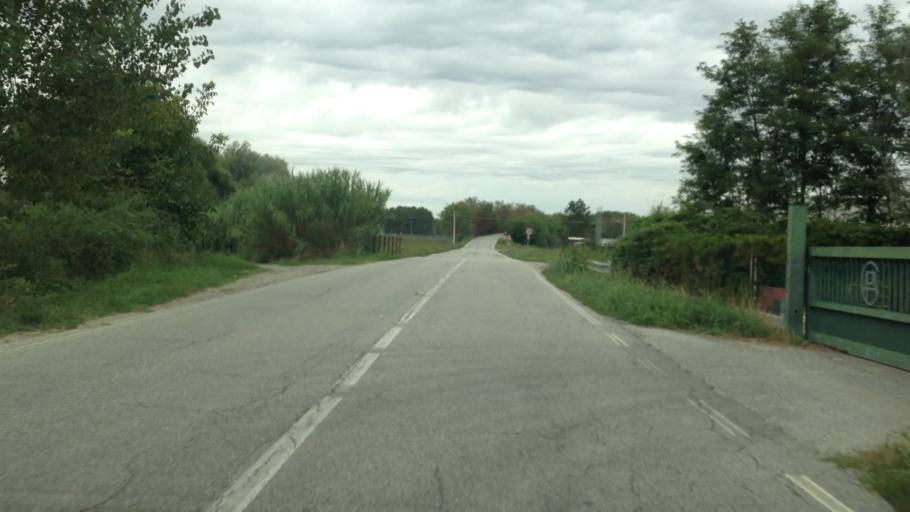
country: IT
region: Piedmont
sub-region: Provincia di Alessandria
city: Quattordio
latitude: 44.9045
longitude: 8.4026
